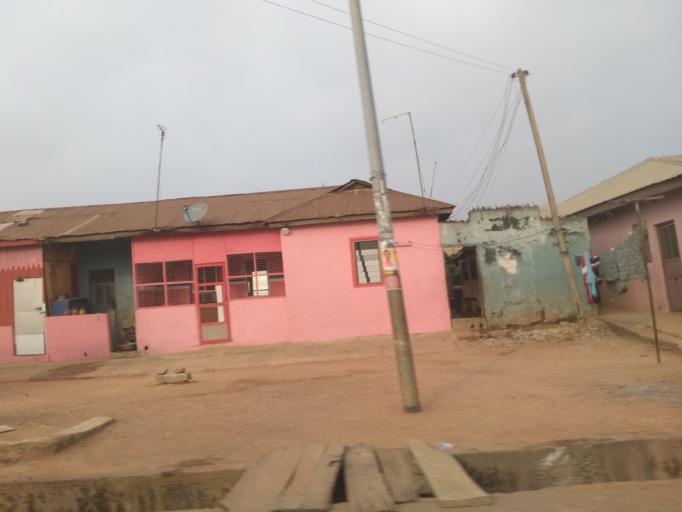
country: GH
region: Ashanti
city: Kumasi
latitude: 6.6869
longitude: -1.5902
